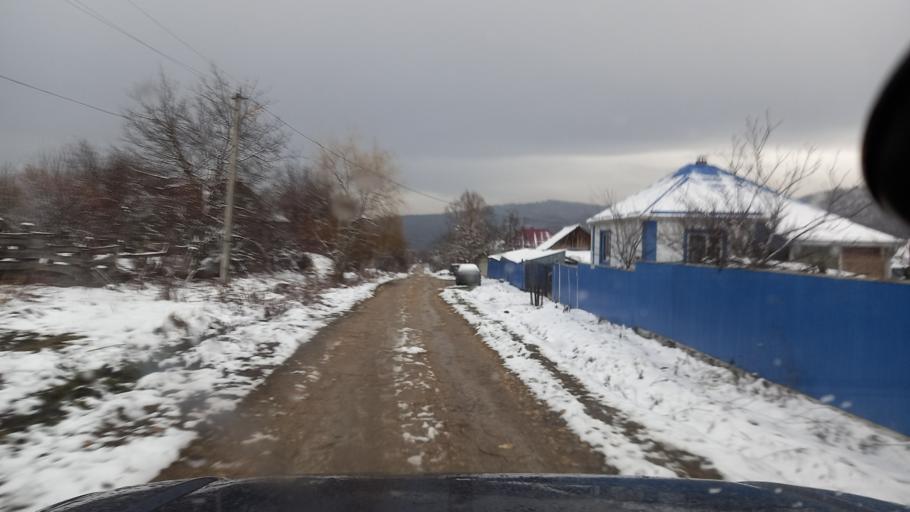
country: RU
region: Adygeya
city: Abadzekhskaya
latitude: 44.3552
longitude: 40.4097
